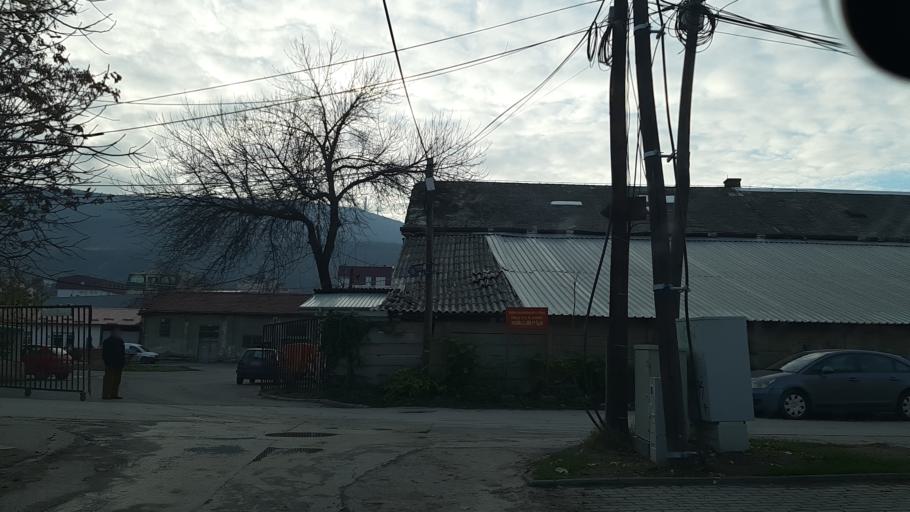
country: MK
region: Karpos
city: Skopje
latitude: 41.9832
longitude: 21.4417
